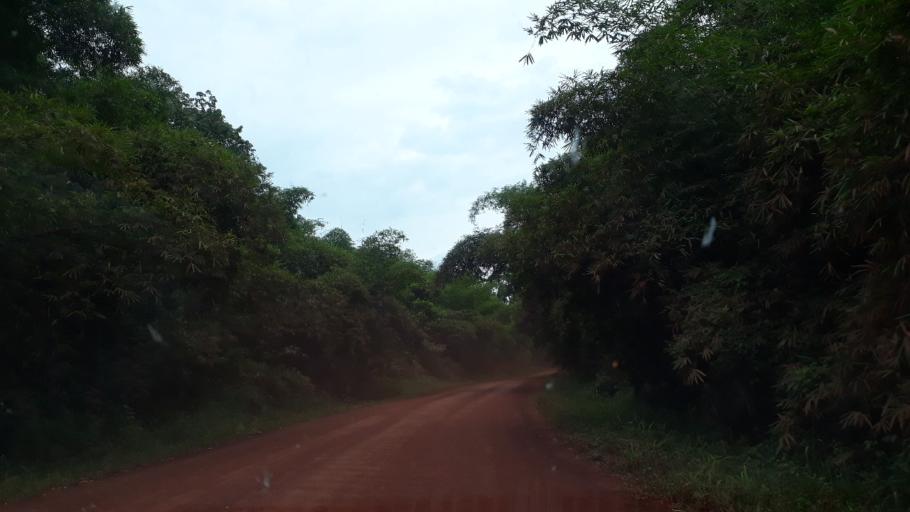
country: CD
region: Eastern Province
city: Kisangani
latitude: 0.5454
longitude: 25.9200
